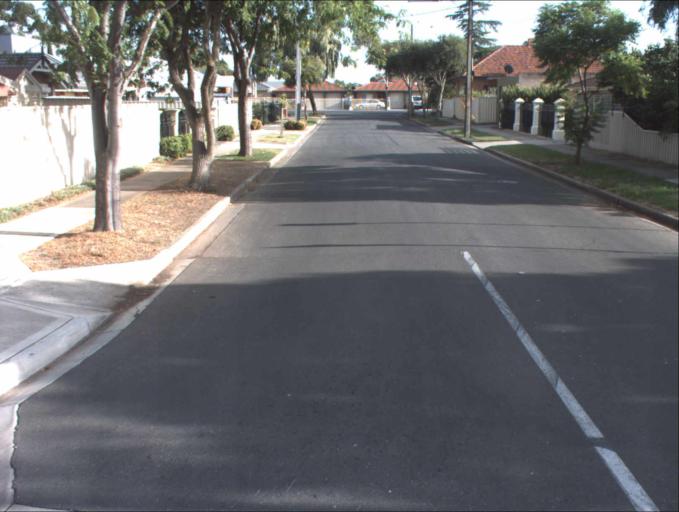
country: AU
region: South Australia
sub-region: Port Adelaide Enfield
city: Klemzig
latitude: -34.8726
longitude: 138.6280
